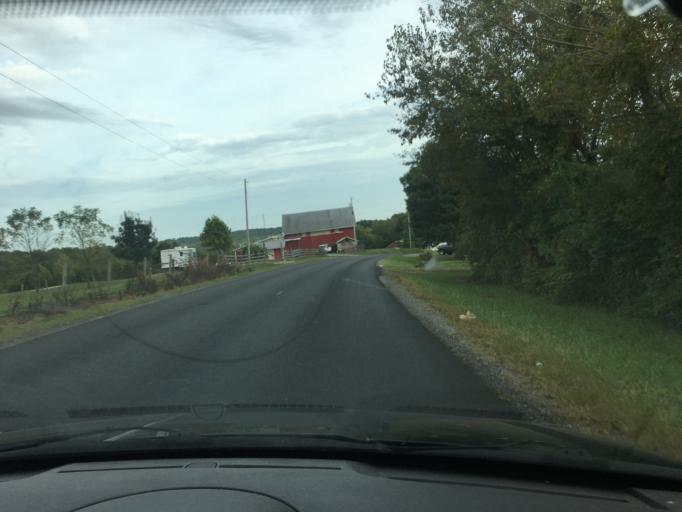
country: US
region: Ohio
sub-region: Logan County
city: Bellefontaine
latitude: 40.3164
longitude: -83.7130
